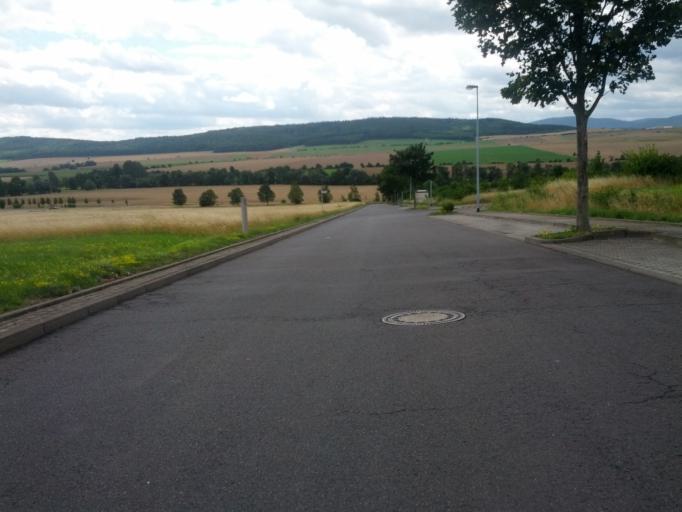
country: DE
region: Thuringia
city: Bischofroda
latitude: 50.9967
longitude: 10.3977
